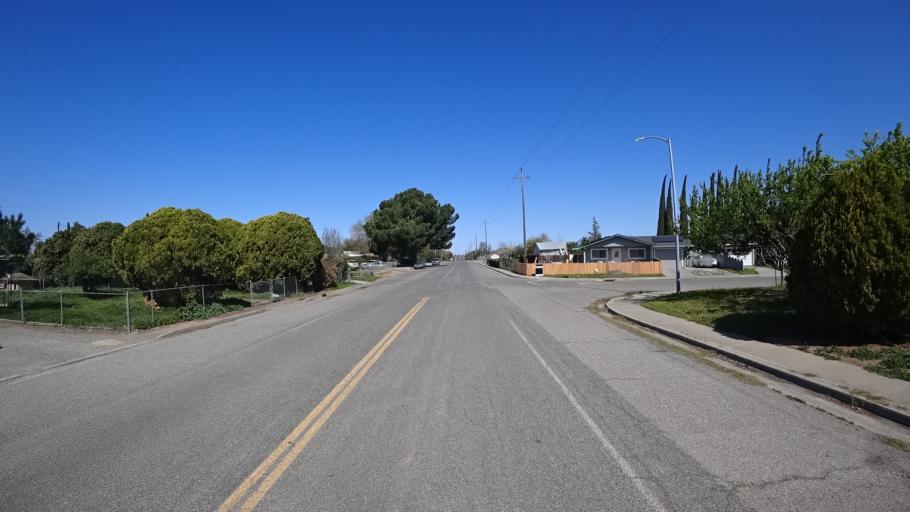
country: US
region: California
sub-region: Glenn County
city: Hamilton City
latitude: 39.7416
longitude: -122.0065
